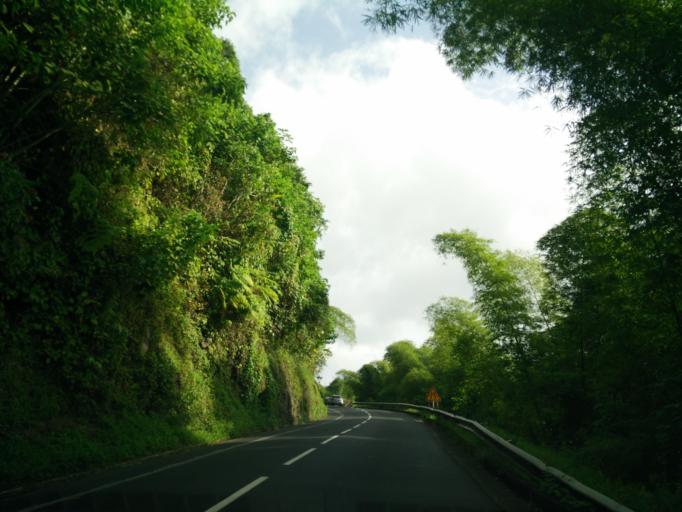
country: MQ
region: Martinique
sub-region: Martinique
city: Le Morne-Rouge
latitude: 14.7634
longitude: -61.1576
